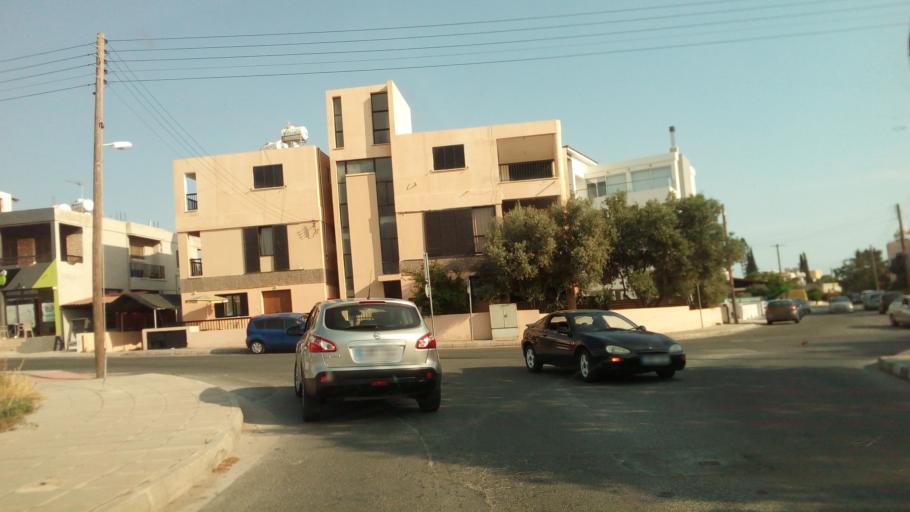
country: CY
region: Pafos
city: Paphos
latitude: 34.7711
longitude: 32.4157
